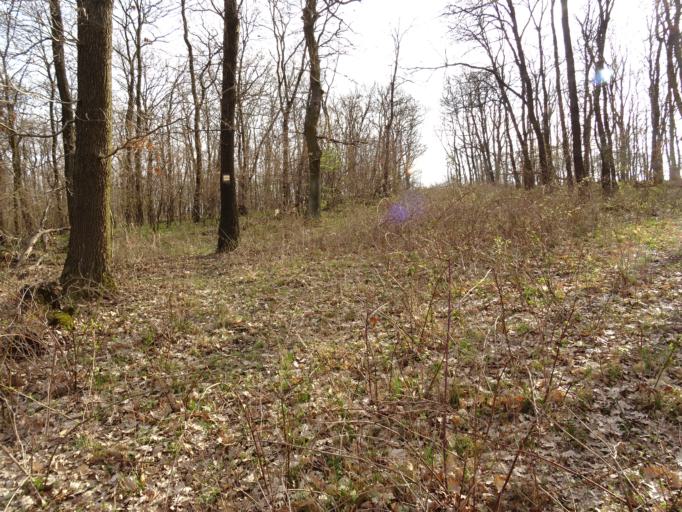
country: HU
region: Fejer
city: Lovasbereny
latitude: 47.2692
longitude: 18.5953
